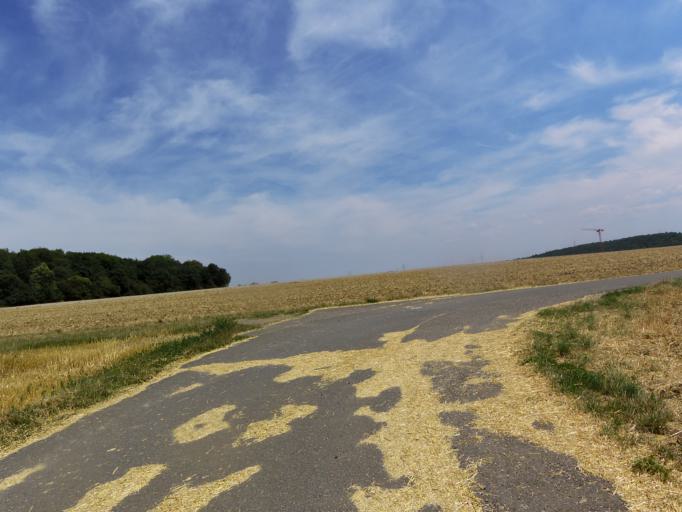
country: DE
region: Bavaria
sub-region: Regierungsbezirk Unterfranken
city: Rottendorf
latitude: 49.8075
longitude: 10.0366
